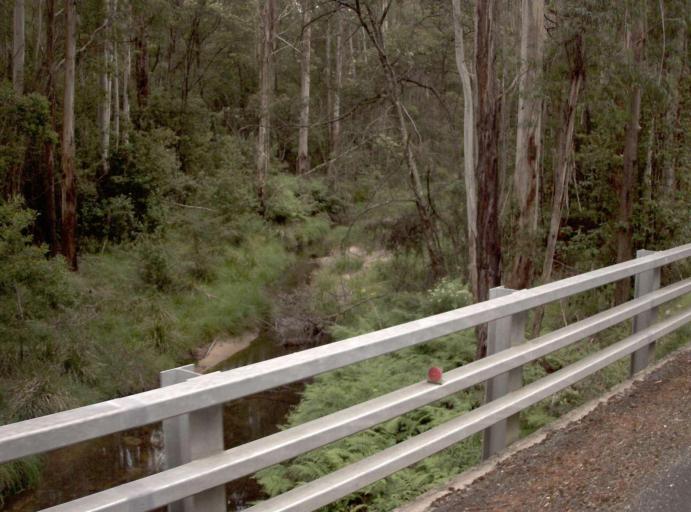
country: AU
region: New South Wales
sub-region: Bombala
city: Bombala
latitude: -37.2833
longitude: 149.2222
